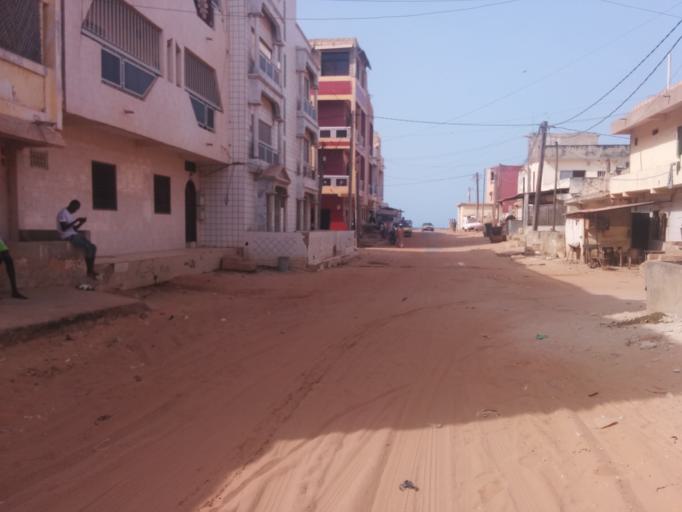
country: SN
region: Dakar
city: Pikine
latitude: 14.7652
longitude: -17.4397
